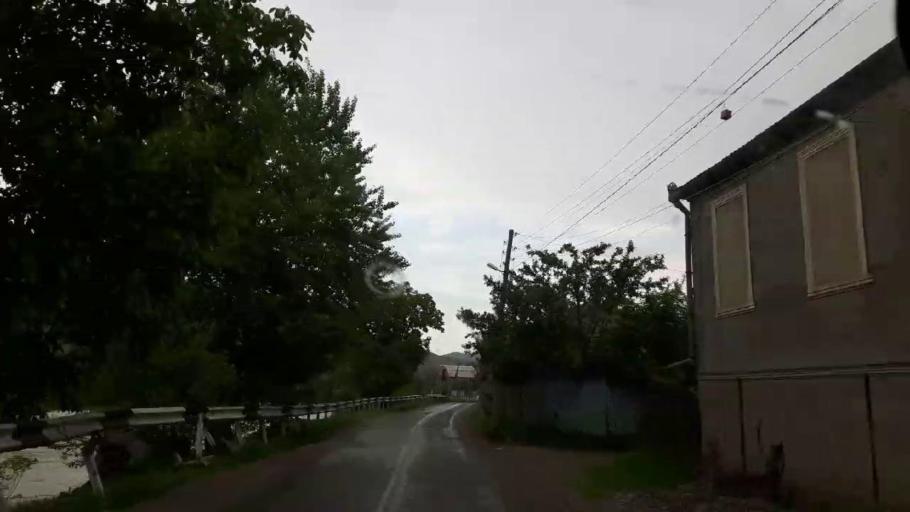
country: GE
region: Shida Kartli
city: Gori
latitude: 41.9666
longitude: 44.2160
